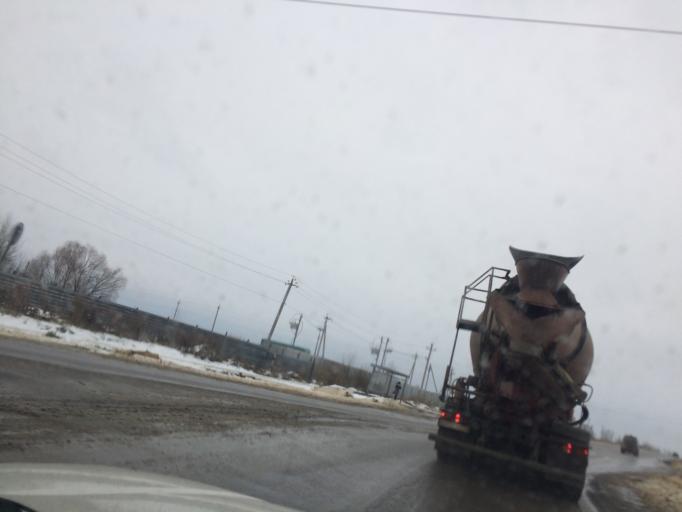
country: RU
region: Tula
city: Kosaya Gora
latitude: 54.1642
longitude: 37.4651
